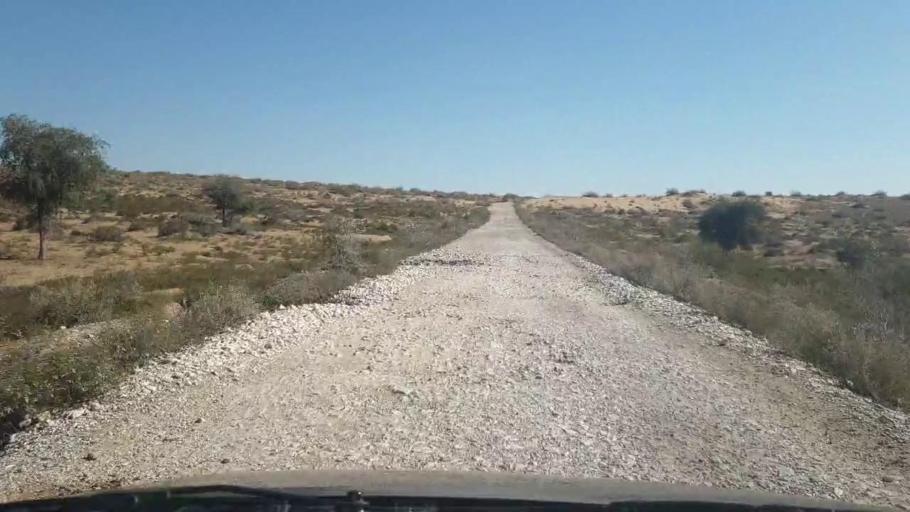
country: PK
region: Sindh
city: Bozdar
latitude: 27.0188
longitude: 68.7311
